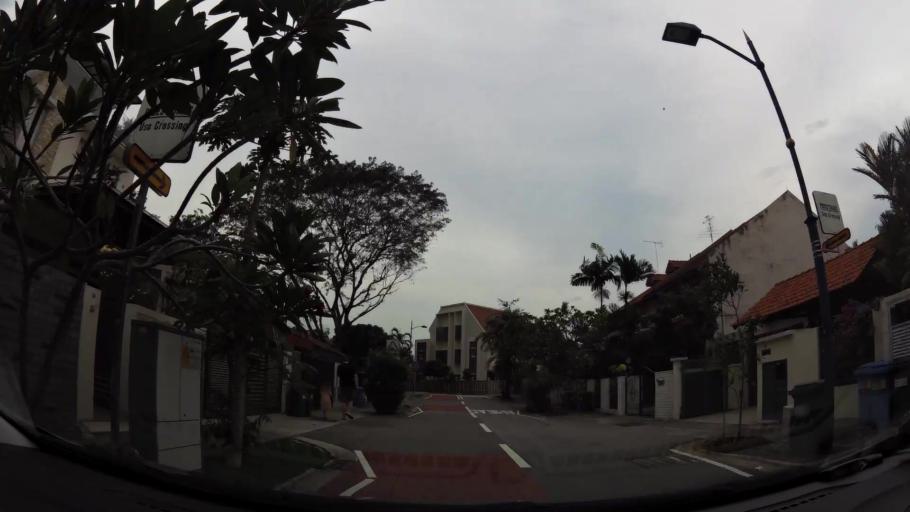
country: SG
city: Singapore
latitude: 1.3682
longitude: 103.8670
